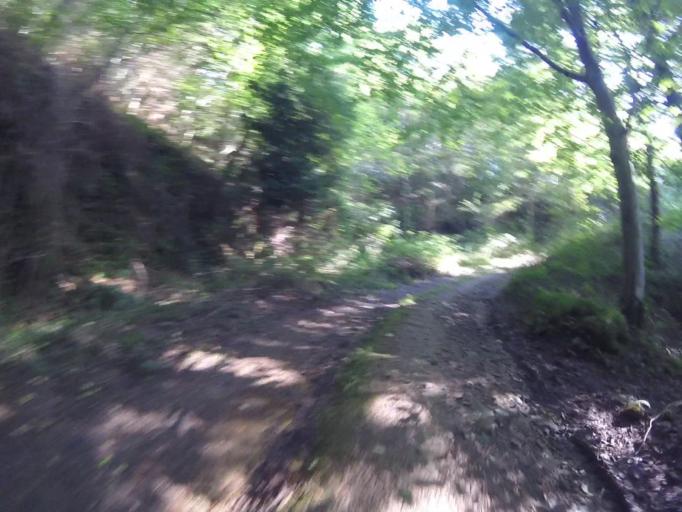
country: ES
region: Navarre
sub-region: Provincia de Navarra
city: Arano
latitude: 43.2467
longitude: -1.9005
